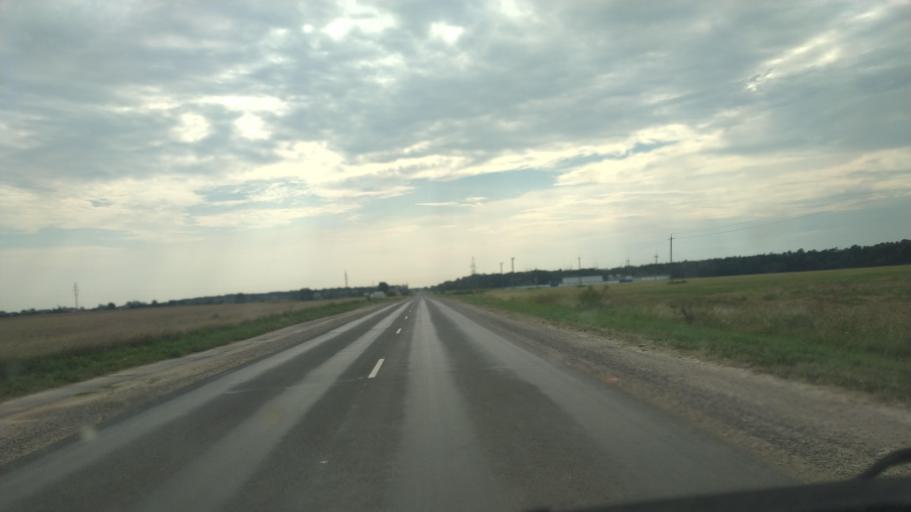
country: BY
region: Brest
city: Byaroza
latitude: 52.5497
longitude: 24.9430
